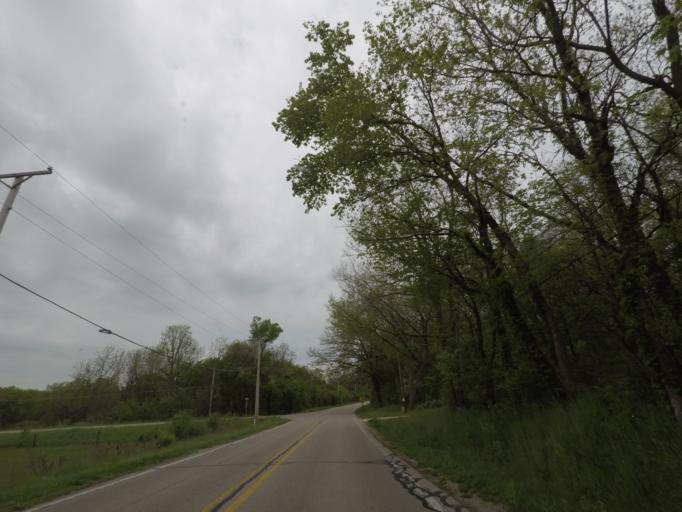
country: US
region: Illinois
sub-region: Winnebago County
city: Roscoe
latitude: 42.4169
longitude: -88.9768
